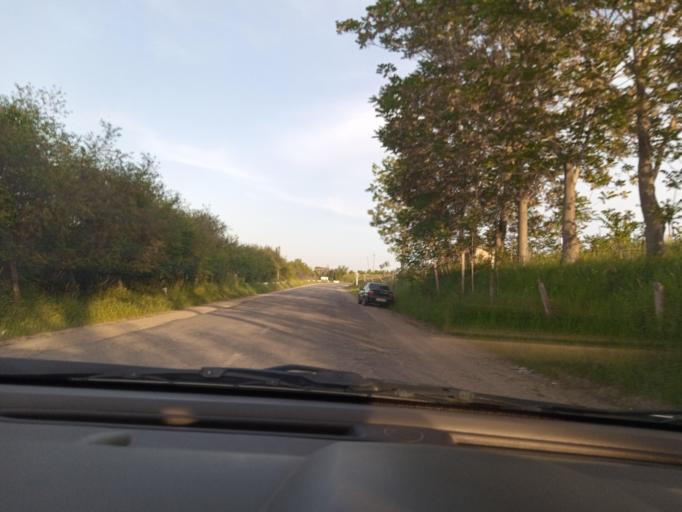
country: UZ
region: Toshkent
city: Parkent
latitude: 41.2367
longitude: 69.7358
